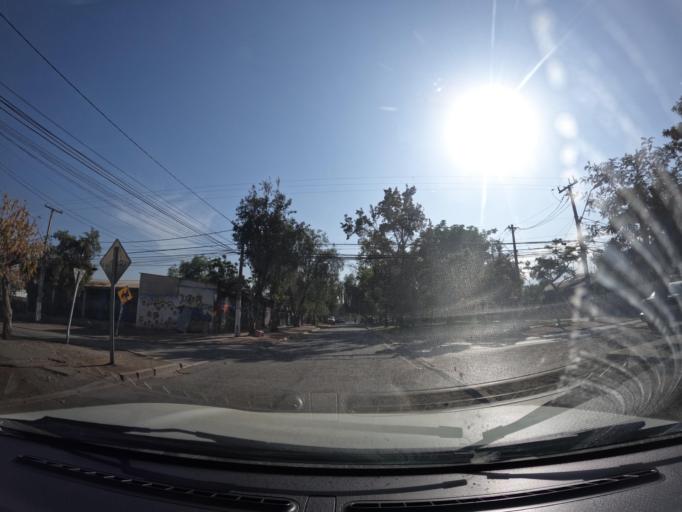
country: CL
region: Santiago Metropolitan
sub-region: Provincia de Santiago
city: Villa Presidente Frei, Nunoa, Santiago, Chile
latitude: -33.4698
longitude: -70.5653
